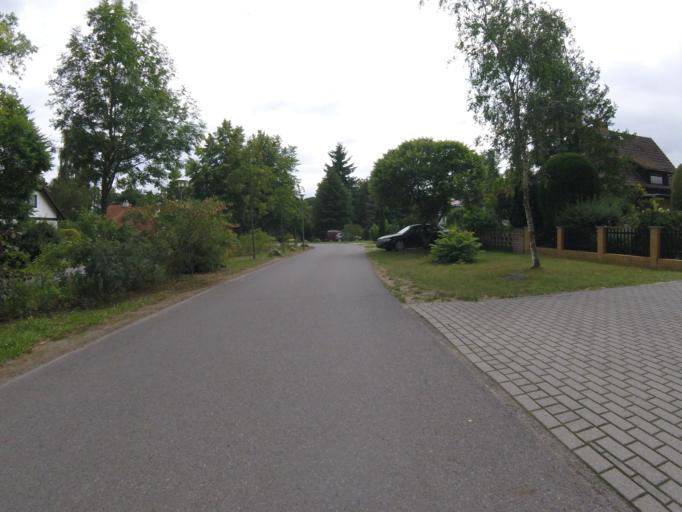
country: DE
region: Brandenburg
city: Konigs Wusterhausen
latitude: 52.2963
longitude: 13.6122
